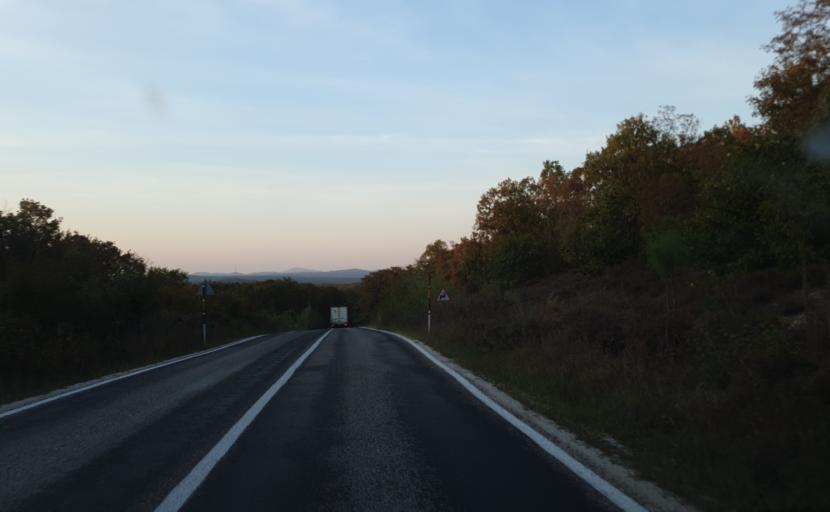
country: TR
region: Kirklareli
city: Igneada
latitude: 41.8682
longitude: 27.8862
